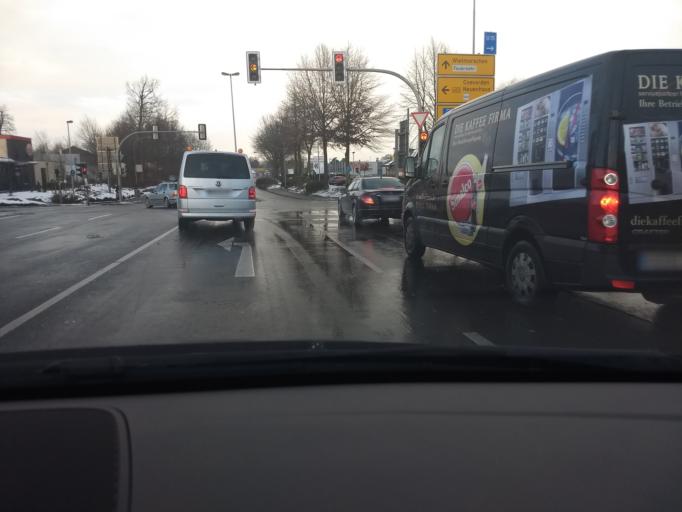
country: DE
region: Lower Saxony
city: Nordhorn
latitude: 52.4404
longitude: 7.0839
